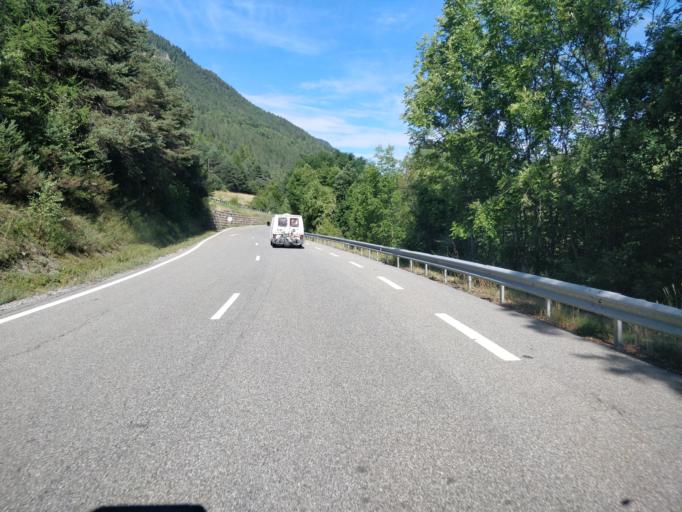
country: FR
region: Provence-Alpes-Cote d'Azur
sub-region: Departement des Alpes-de-Haute-Provence
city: Seyne-les-Alpes
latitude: 44.4232
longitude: 6.4424
